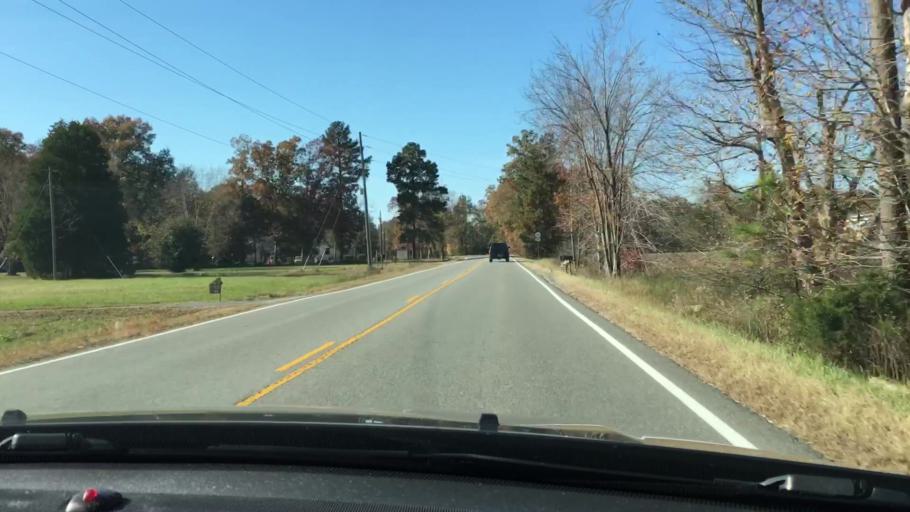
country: US
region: Virginia
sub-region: Hanover County
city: Hanover
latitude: 37.8303
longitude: -77.3535
